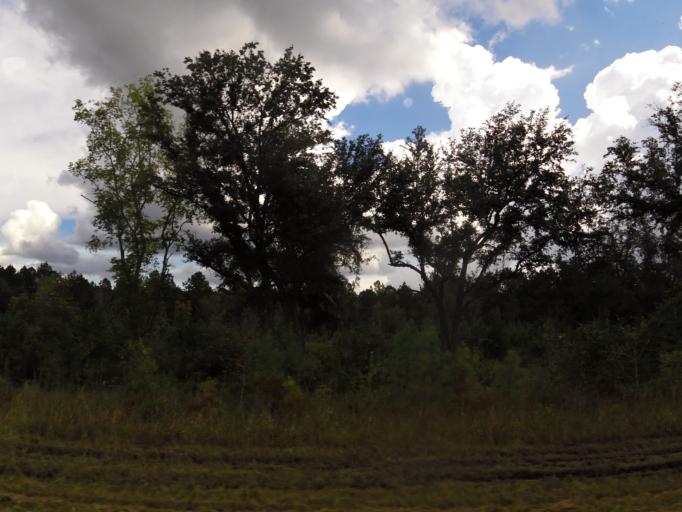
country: US
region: Georgia
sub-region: Charlton County
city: Folkston
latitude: 31.0069
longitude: -82.0270
